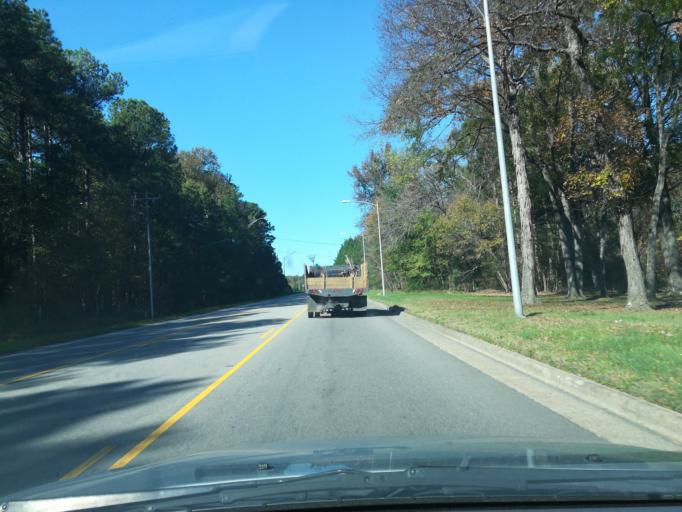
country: US
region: North Carolina
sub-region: Durham County
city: Durham
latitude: 36.0259
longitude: -78.9578
